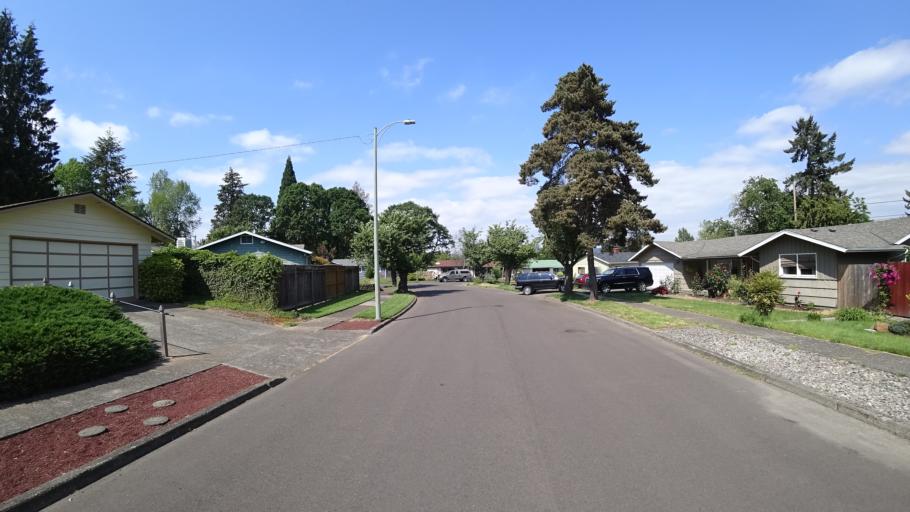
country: US
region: Oregon
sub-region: Washington County
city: Beaverton
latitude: 45.4722
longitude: -122.7928
